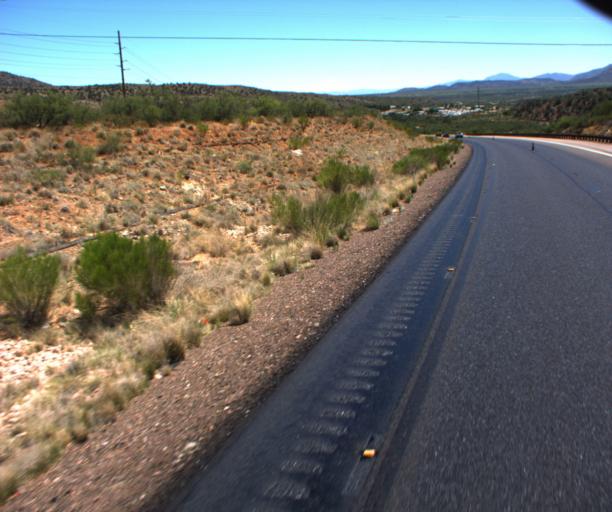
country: US
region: Arizona
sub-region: Gila County
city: Payson
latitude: 34.1193
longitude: -111.3572
